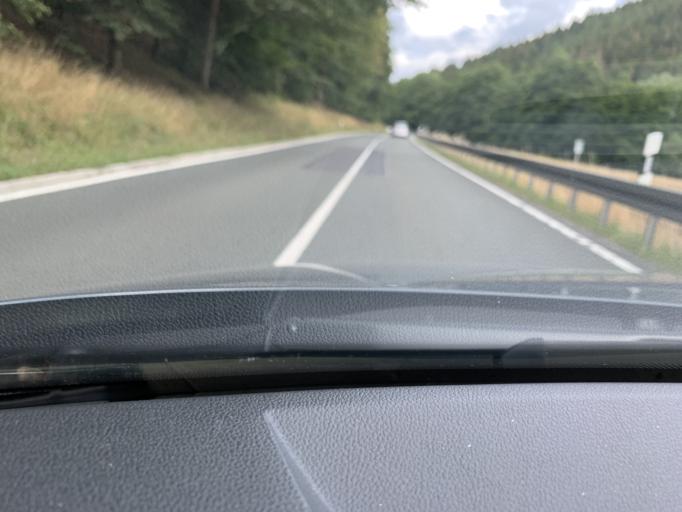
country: DE
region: Thuringia
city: Judenbach
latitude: 50.4059
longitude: 11.1880
